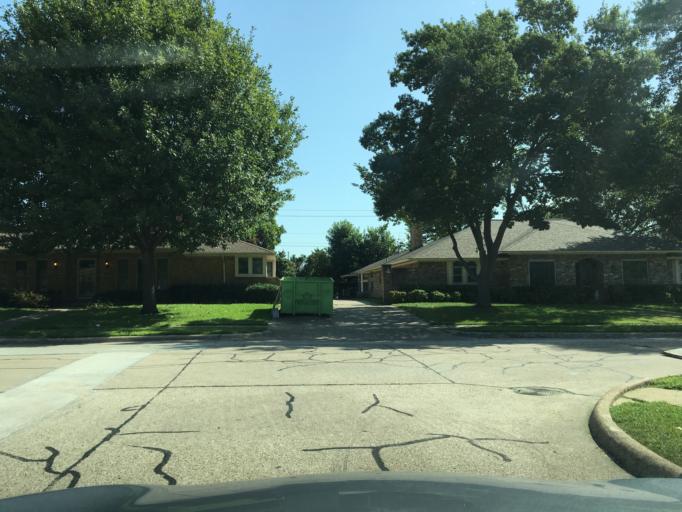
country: US
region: Texas
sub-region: Dallas County
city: Garland
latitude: 32.8747
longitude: -96.6229
